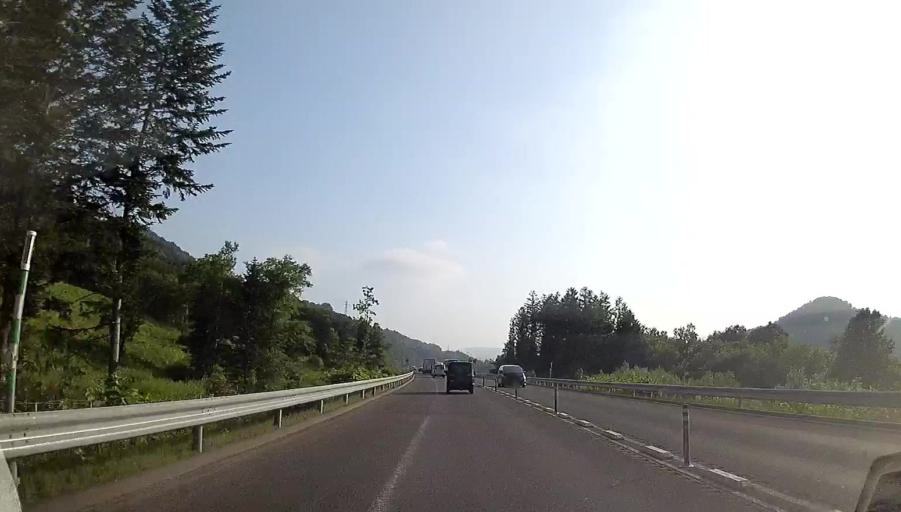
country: JP
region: Hokkaido
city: Shimo-furano
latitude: 43.0193
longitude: 142.4366
